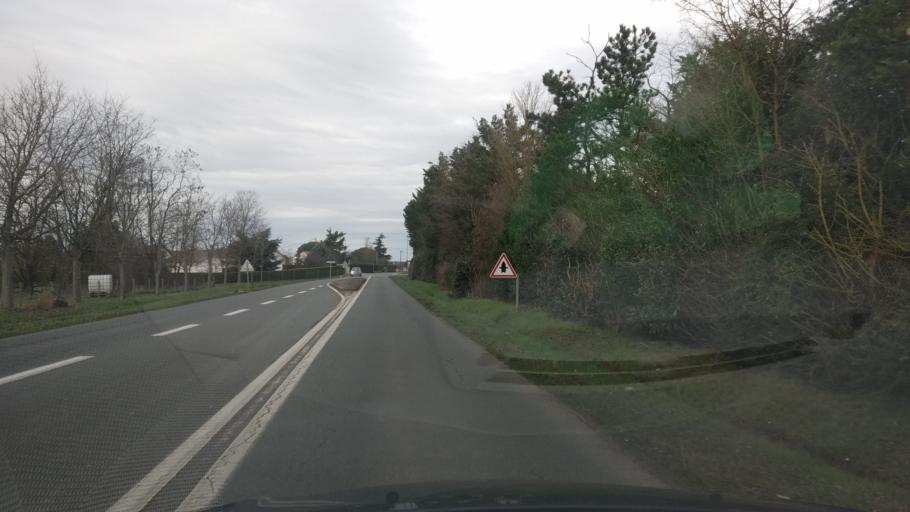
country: FR
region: Poitou-Charentes
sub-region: Departement de la Vienne
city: Saint-Georges-les-Baillargeaux
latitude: 46.6861
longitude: 0.4155
